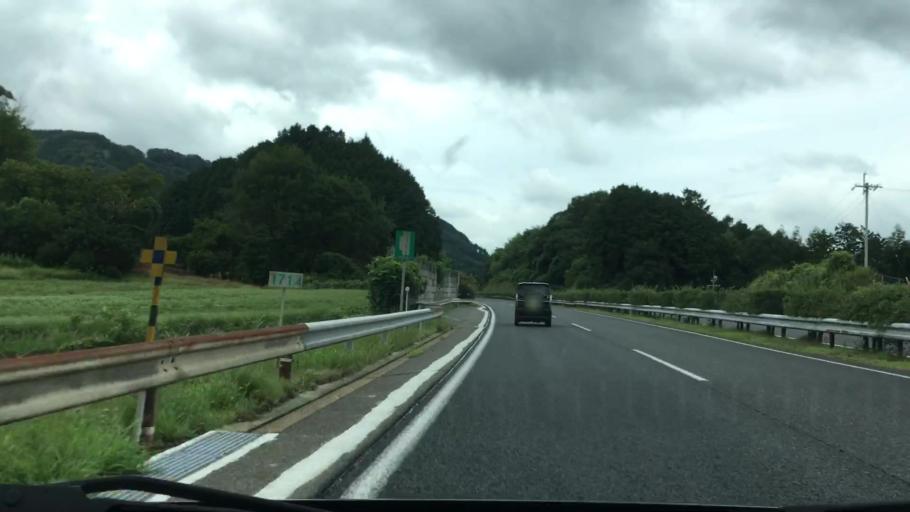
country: JP
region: Okayama
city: Tsuyama
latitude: 35.0628
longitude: 133.8446
